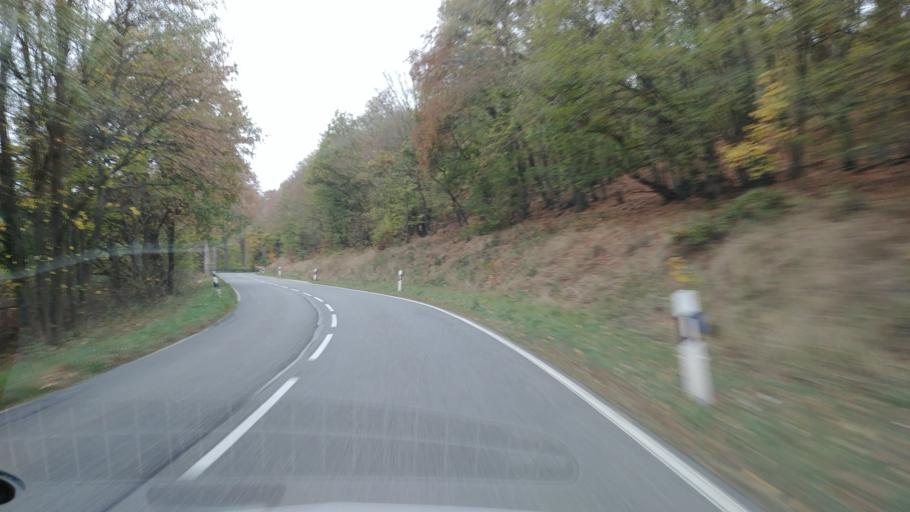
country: DE
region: Hesse
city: Taunusstein
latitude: 50.1529
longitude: 8.1610
